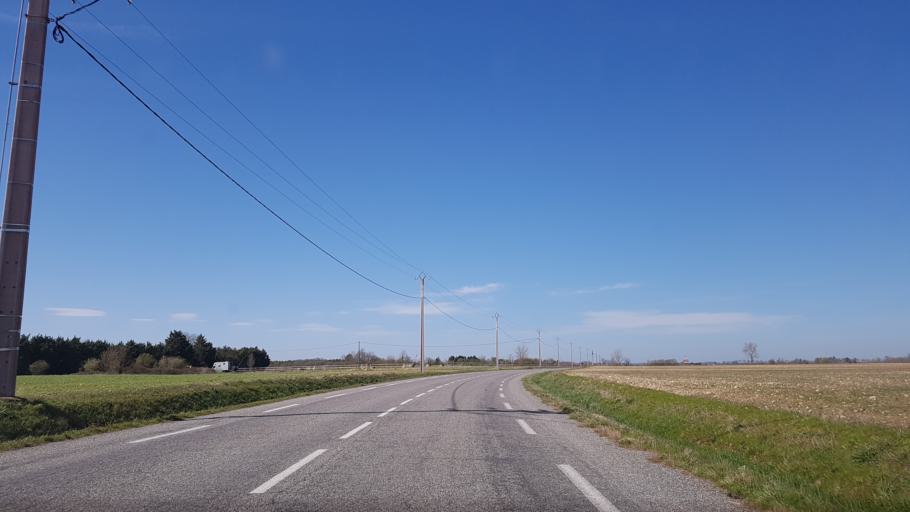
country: FR
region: Midi-Pyrenees
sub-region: Departement de l'Ariege
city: Mazeres
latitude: 43.2276
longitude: 1.6788
